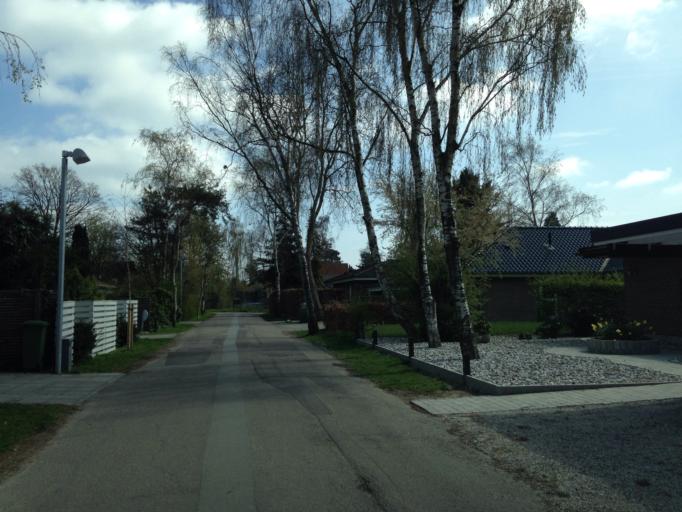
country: DK
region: Zealand
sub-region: Greve Kommune
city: Greve
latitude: 55.5766
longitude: 12.2923
